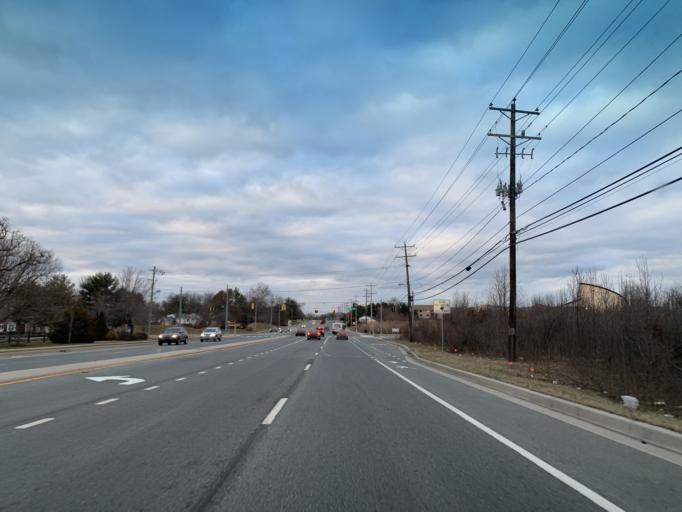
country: US
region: Delaware
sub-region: New Castle County
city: Bear
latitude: 39.6487
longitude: -75.6562
